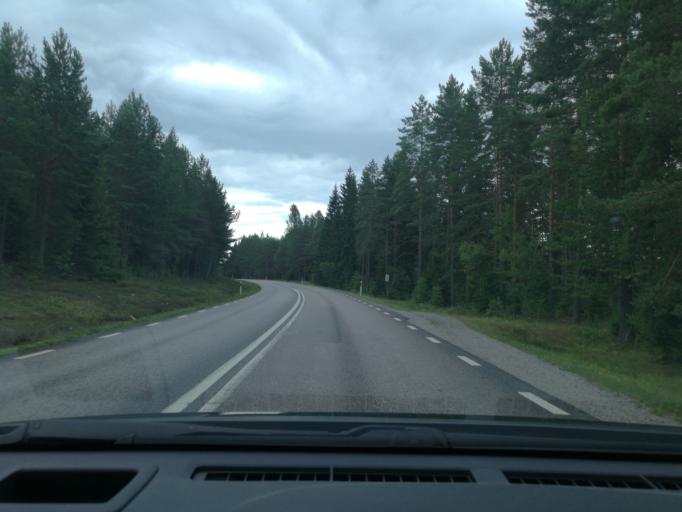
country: SE
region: Soedermanland
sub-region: Katrineholms Kommun
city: Katrineholm
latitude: 59.1066
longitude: 16.1778
